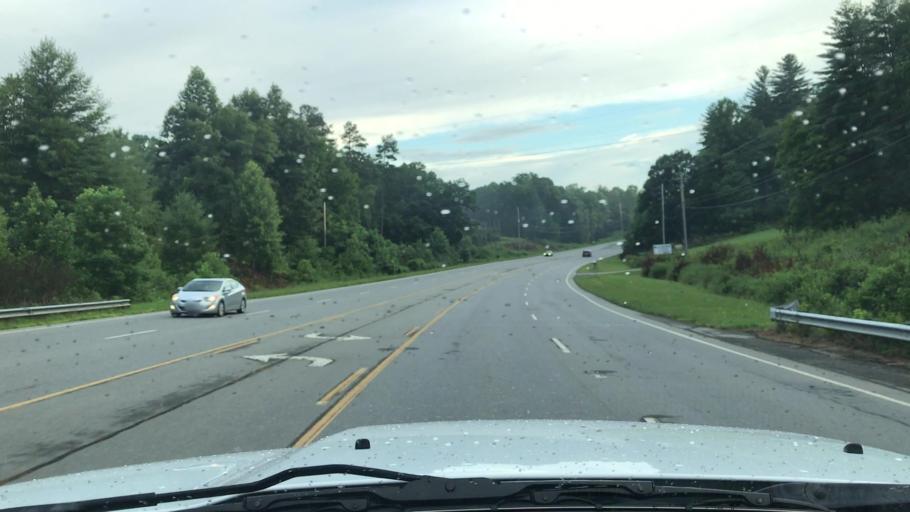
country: US
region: North Carolina
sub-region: Cherokee County
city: Murphy
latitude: 35.0138
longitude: -84.1236
